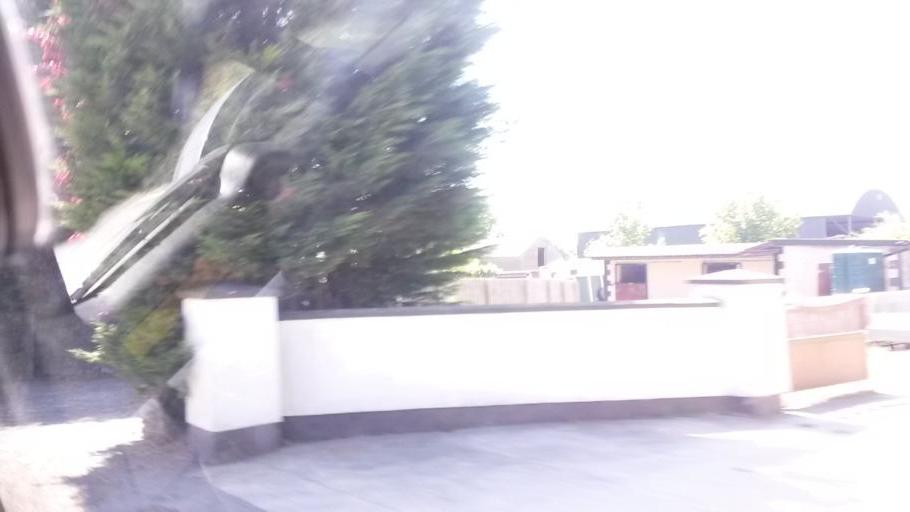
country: IE
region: Leinster
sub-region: An Mhi
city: Stamullin
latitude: 53.5795
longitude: -6.3103
